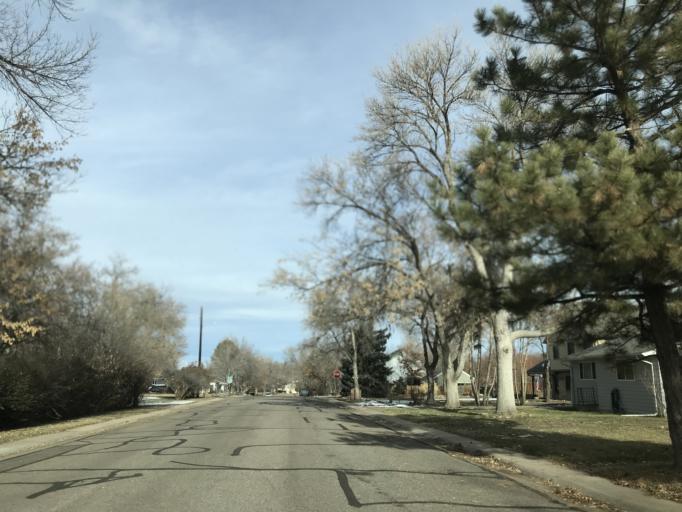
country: US
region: Colorado
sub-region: Arapahoe County
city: Littleton
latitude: 39.6016
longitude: -105.0093
